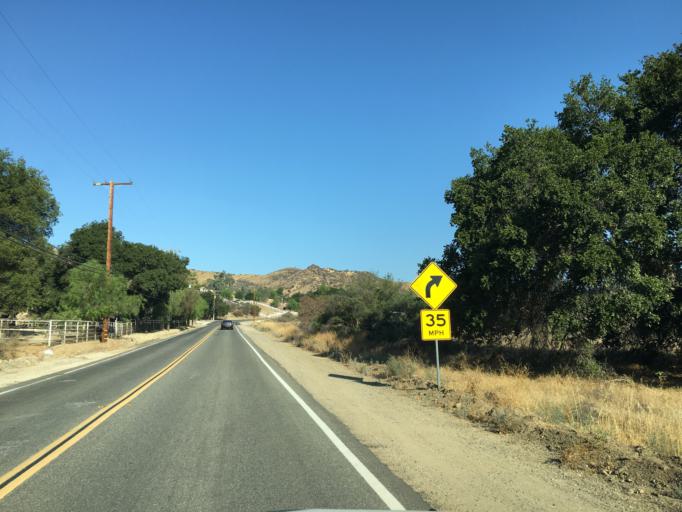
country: US
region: California
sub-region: Los Angeles County
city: Val Verde
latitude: 34.4604
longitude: -118.6553
